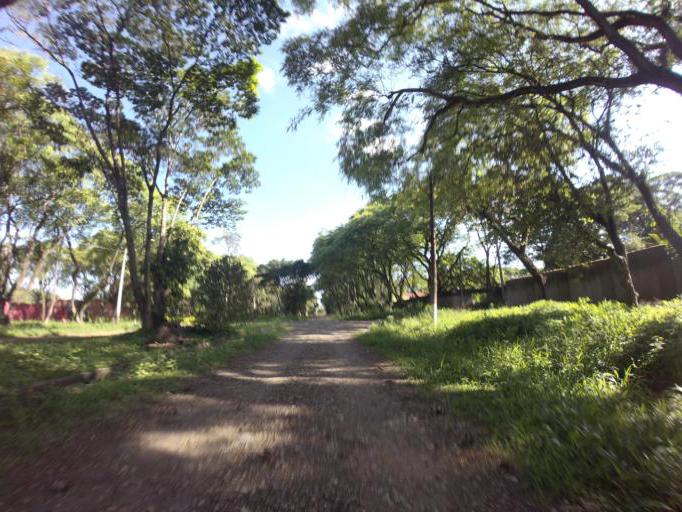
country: BR
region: Sao Paulo
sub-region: Piracicaba
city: Piracicaba
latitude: -22.7498
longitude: -47.5841
